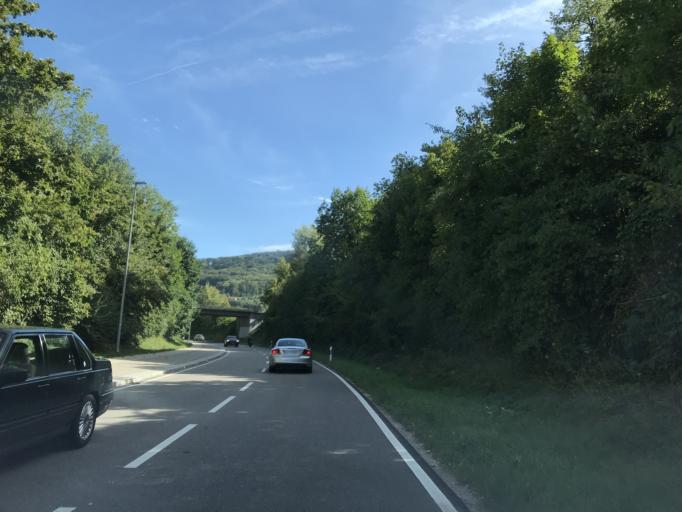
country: DE
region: Baden-Wuerttemberg
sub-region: Freiburg Region
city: Bad Sackingen
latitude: 47.5512
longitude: 7.9364
